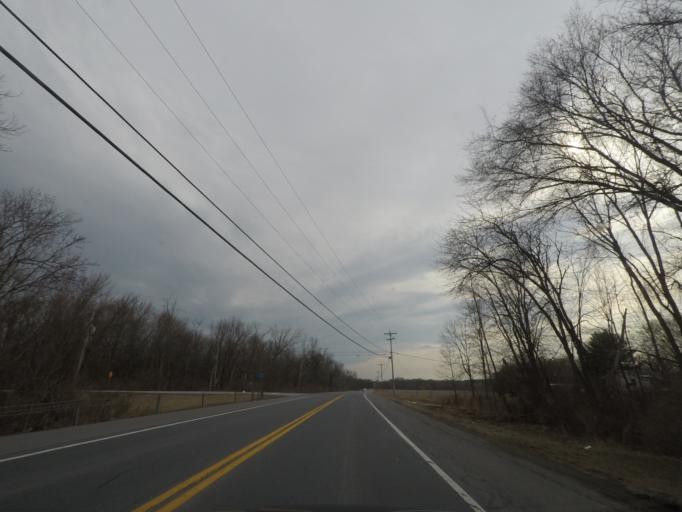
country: US
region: New York
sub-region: Saratoga County
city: Schuylerville
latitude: 43.1511
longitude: -73.5767
